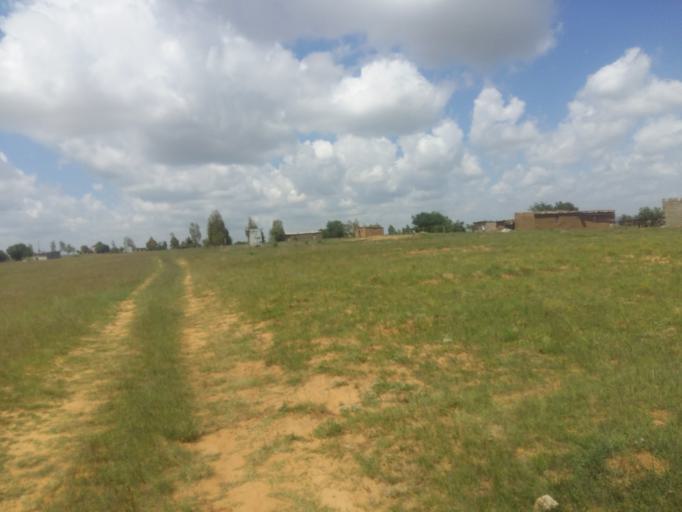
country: LS
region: Mafeteng
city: Mafeteng
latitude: -29.7505
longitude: 27.1139
